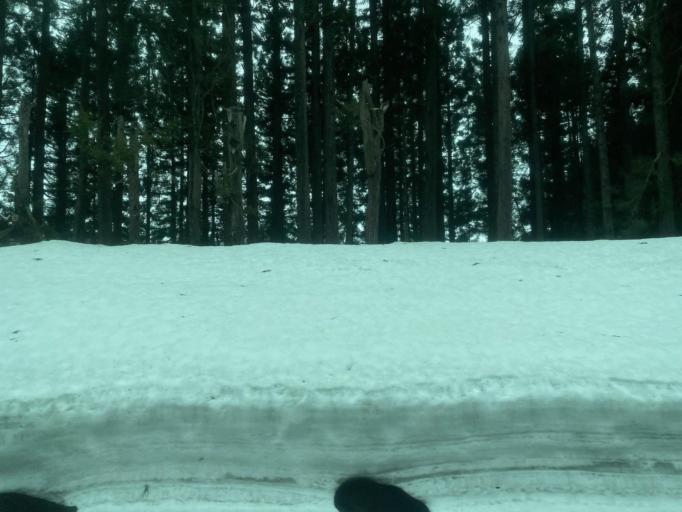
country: JP
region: Niigata
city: Shiozawa
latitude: 36.9225
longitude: 138.8511
